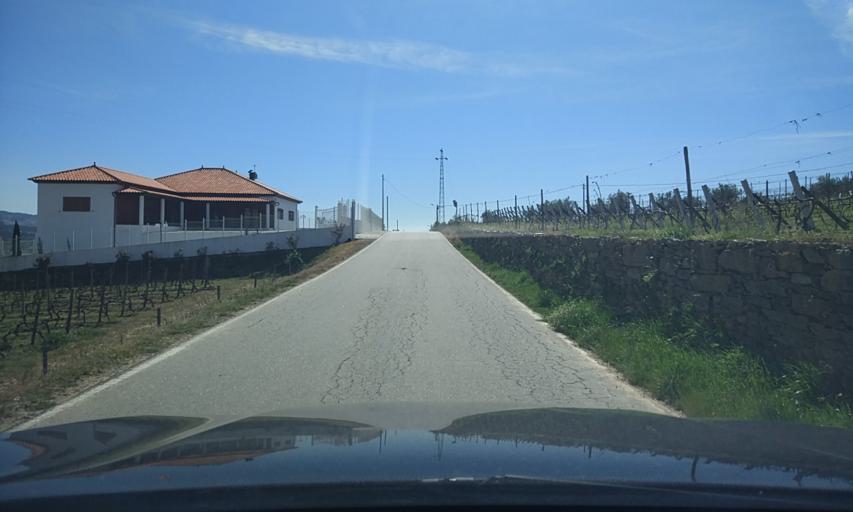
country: PT
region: Vila Real
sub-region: Sabrosa
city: Sabrosa
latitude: 41.3122
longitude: -7.5606
